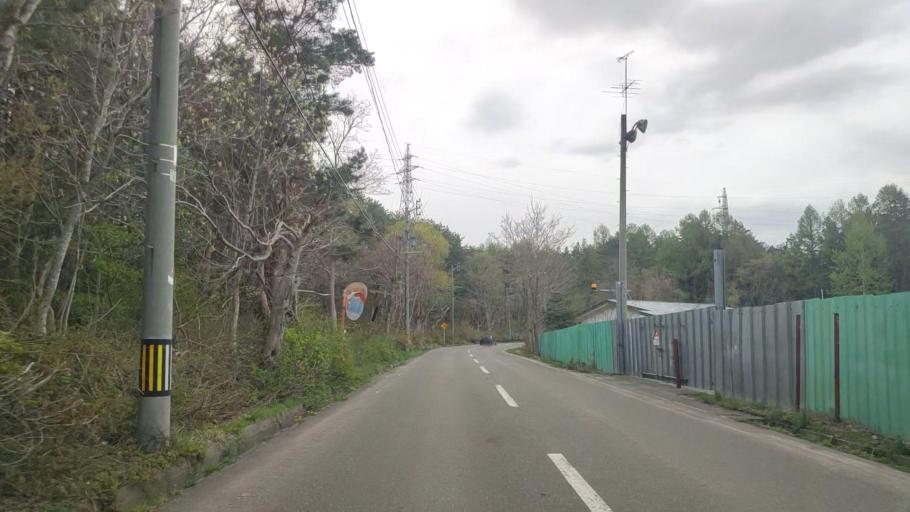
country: JP
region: Aomori
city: Aomori Shi
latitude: 40.7483
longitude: 140.8204
